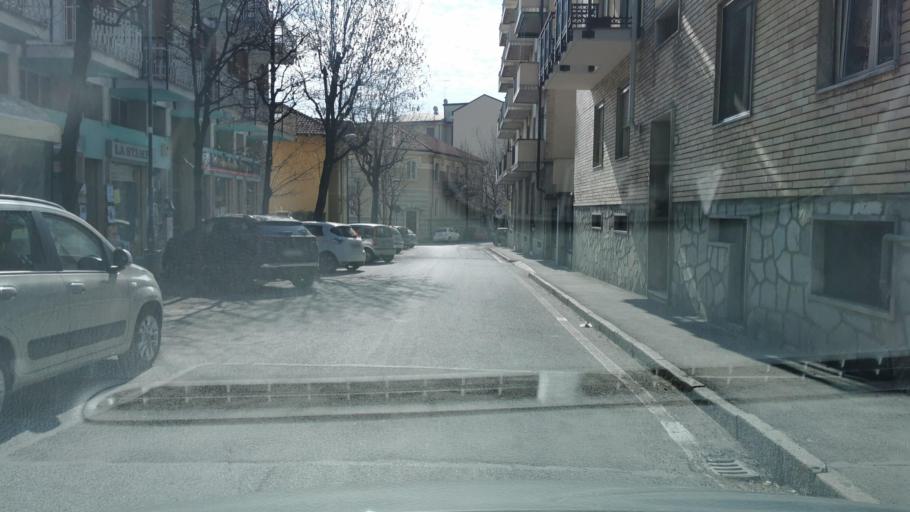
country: IT
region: Piedmont
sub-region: Provincia di Torino
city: Pinerolo
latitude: 44.8912
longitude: 7.3330
